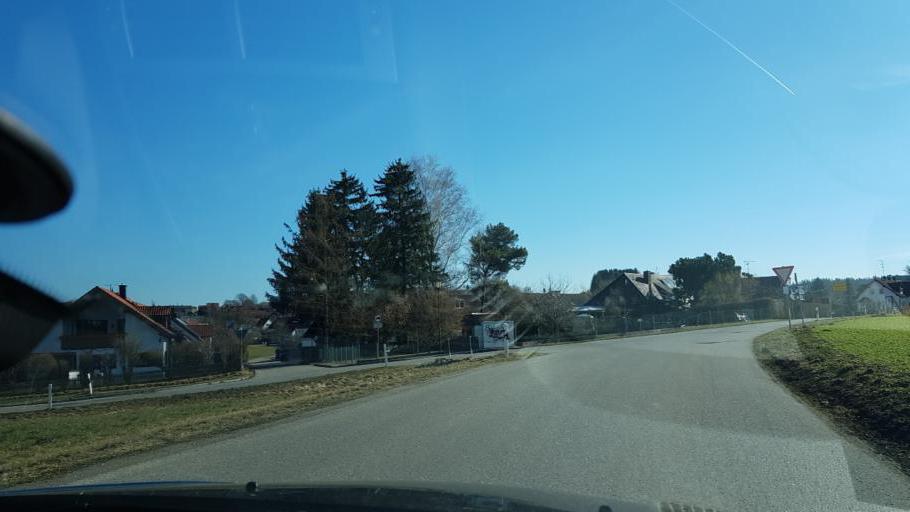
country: DE
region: Bavaria
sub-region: Upper Bavaria
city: Oberschweinbach
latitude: 48.2399
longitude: 11.1531
